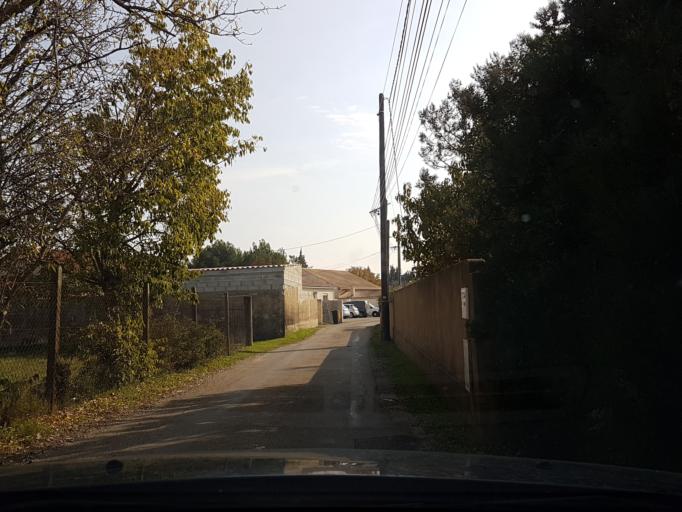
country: FR
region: Provence-Alpes-Cote d'Azur
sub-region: Departement du Vaucluse
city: Sorgues
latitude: 44.0271
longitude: 4.8711
